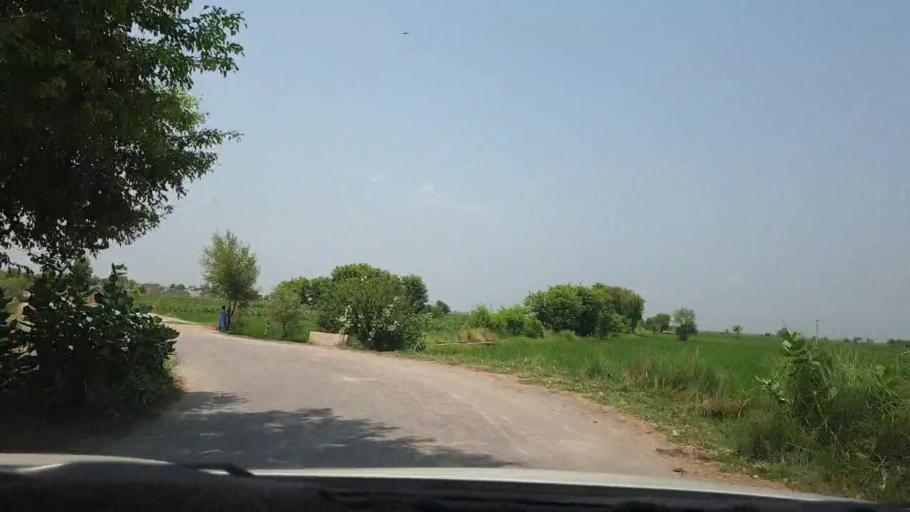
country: PK
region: Sindh
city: Radhan
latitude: 27.2403
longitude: 68.0120
